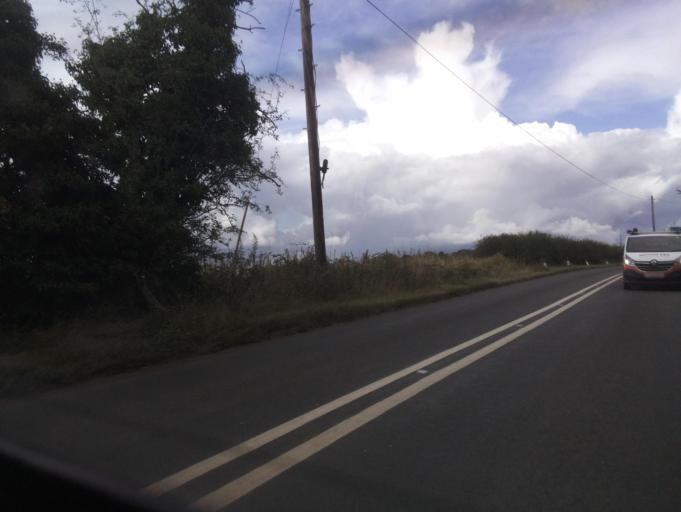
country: GB
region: England
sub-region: Telford and Wrekin
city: Newport
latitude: 52.8020
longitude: -2.3425
